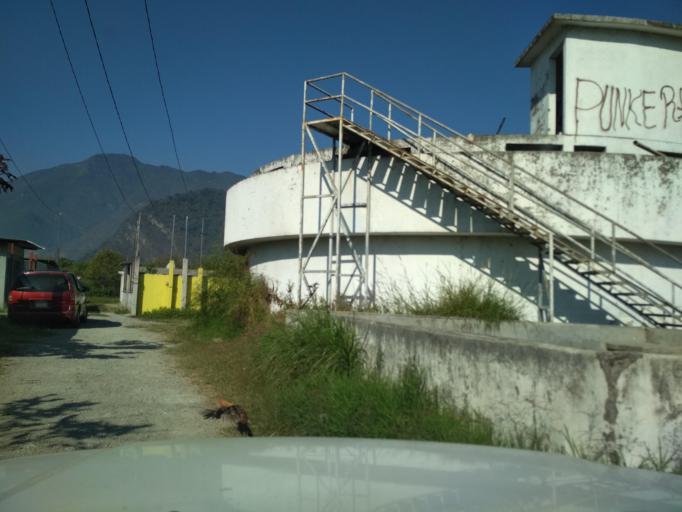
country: MX
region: Veracruz
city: Jalapilla
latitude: 18.8181
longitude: -97.0761
